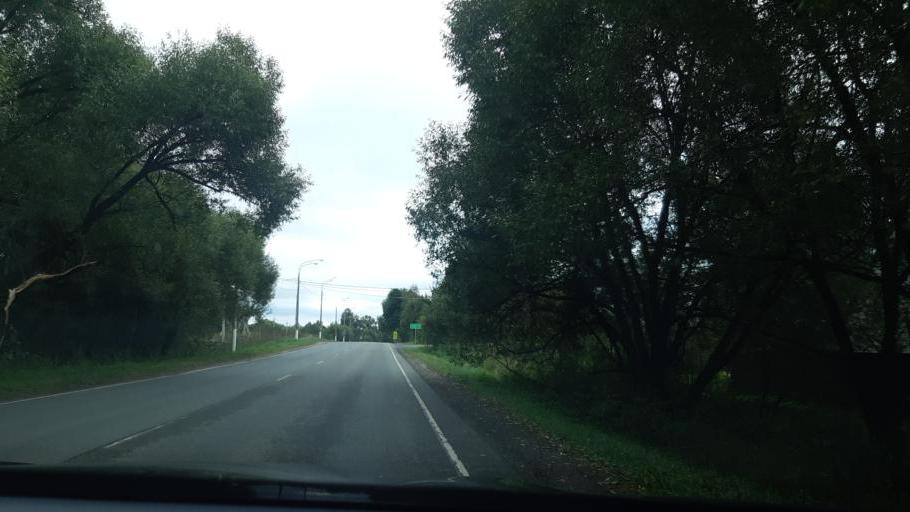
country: RU
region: Moskovskaya
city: Melikhovo
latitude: 55.1148
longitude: 37.6422
